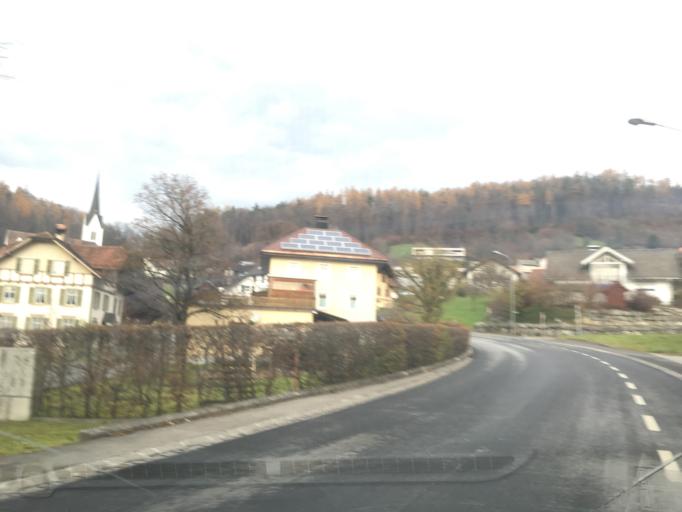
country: AT
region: Vorarlberg
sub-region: Politischer Bezirk Feldkirch
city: Klaus
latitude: 47.3101
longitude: 9.6495
